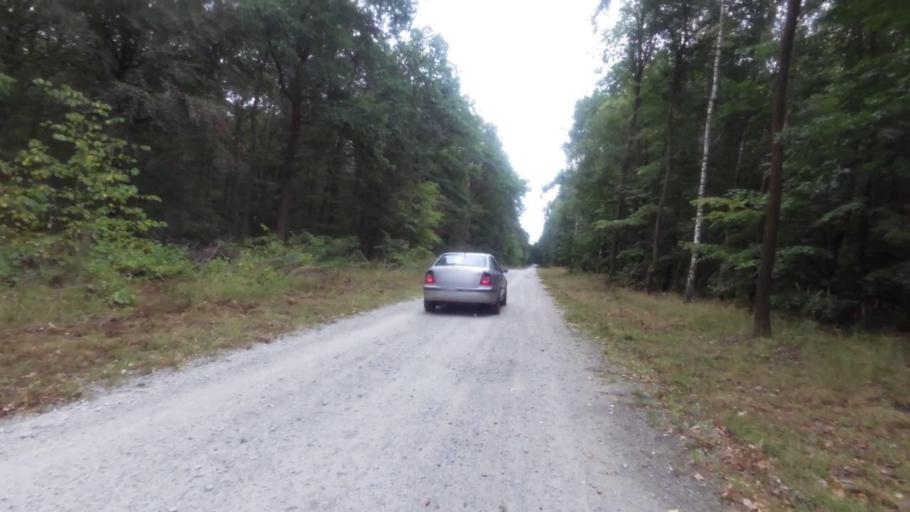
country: PL
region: Lubusz
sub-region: Powiat gorzowski
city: Kostrzyn nad Odra
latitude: 52.6216
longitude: 14.6516
